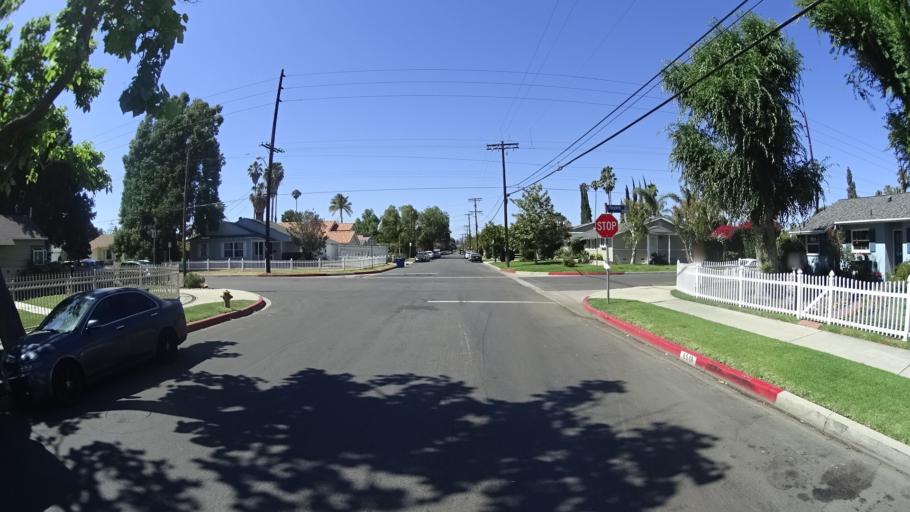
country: US
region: California
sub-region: Los Angeles County
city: Van Nuys
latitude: 34.1889
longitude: -118.4816
